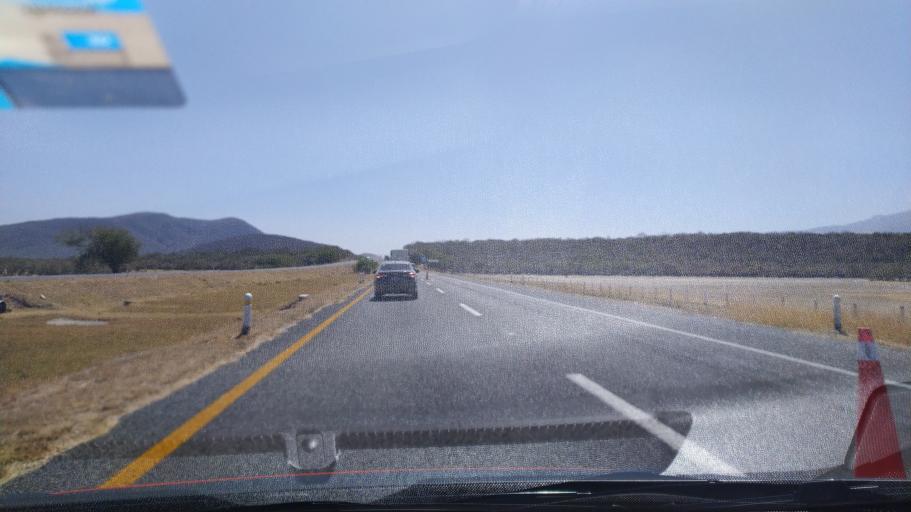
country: MX
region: Jalisco
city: Zacoalco de Torres
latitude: 20.2444
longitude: -103.5398
